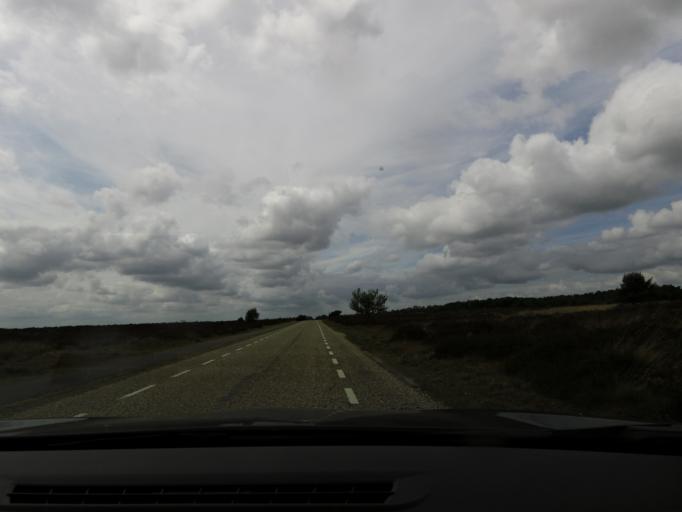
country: NL
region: Gelderland
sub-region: Gemeente Apeldoorn
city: Uddel
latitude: 52.2503
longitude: 5.8130
